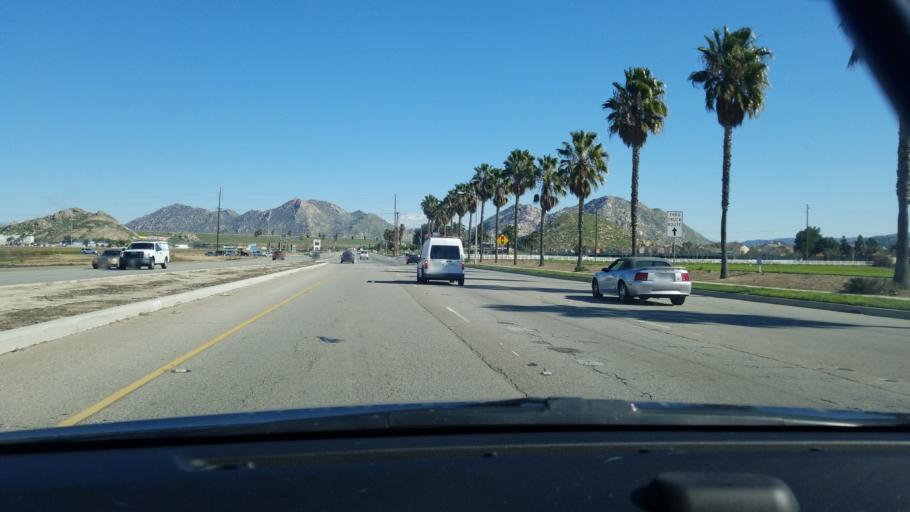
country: US
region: California
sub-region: Riverside County
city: Perris
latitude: 33.8445
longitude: -117.2114
